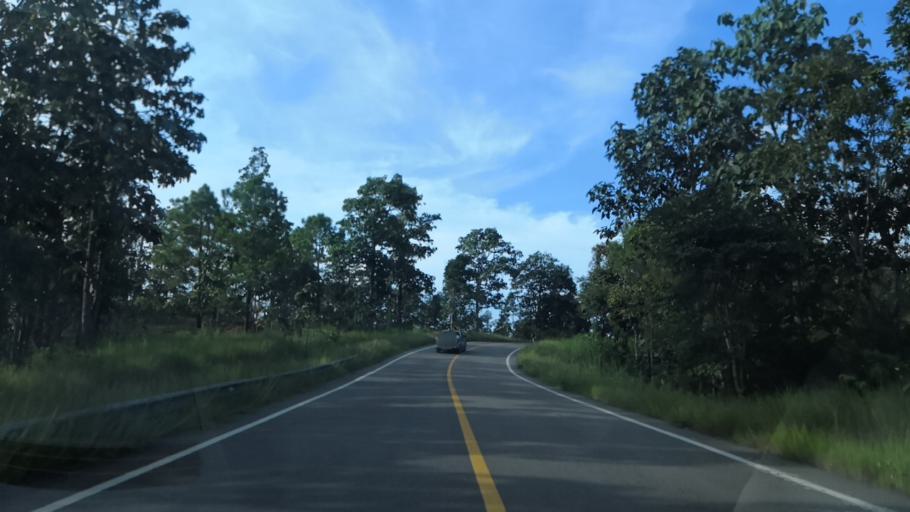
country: TH
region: Mae Hong Son
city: Khun Yuam
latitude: 18.7519
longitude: 97.9272
